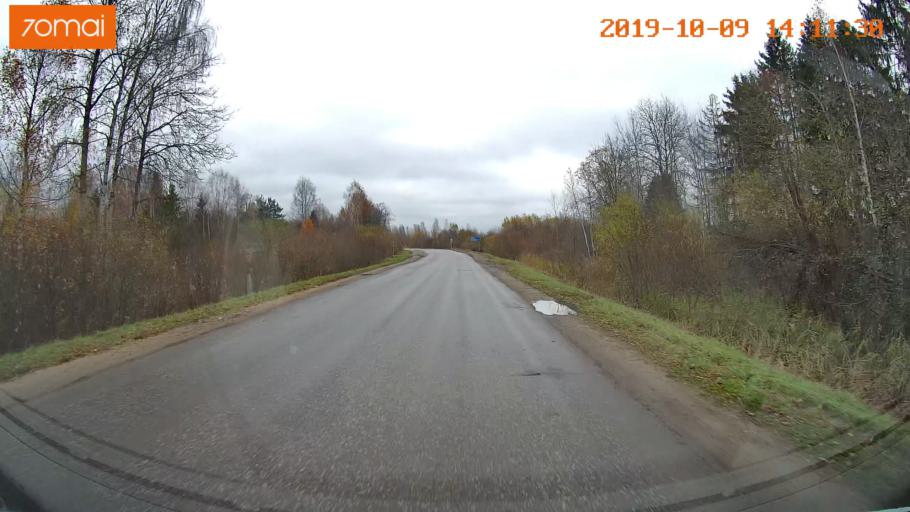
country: RU
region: Kostroma
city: Buy
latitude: 58.4829
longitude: 41.4889
